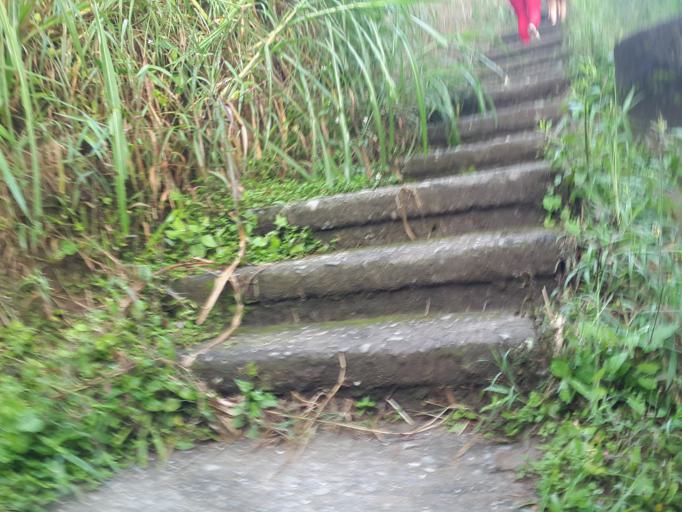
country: CO
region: Quindio
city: Calarca
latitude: 4.5347
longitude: -75.6423
